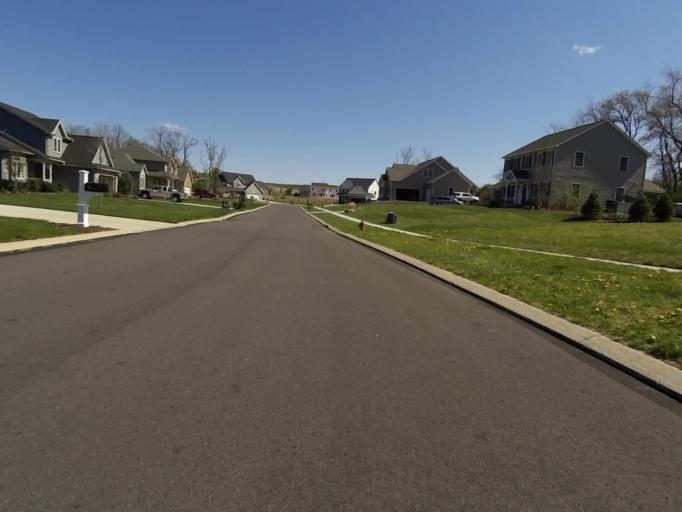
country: US
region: Pennsylvania
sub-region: Centre County
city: Houserville
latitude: 40.8797
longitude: -77.8317
